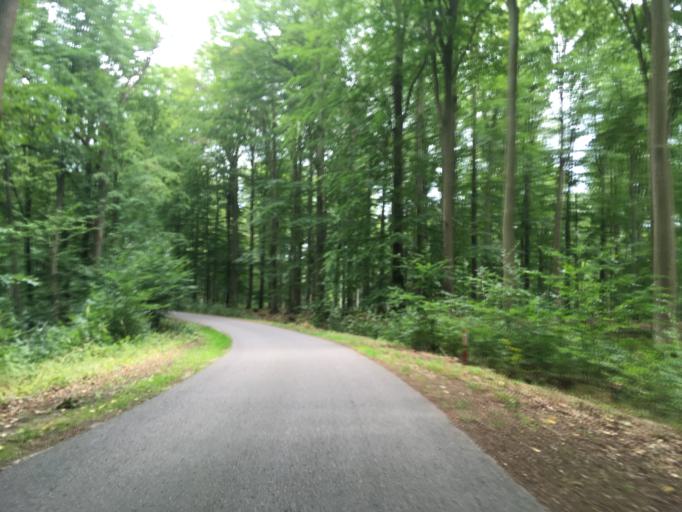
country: DE
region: Brandenburg
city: Althuttendorf
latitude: 53.0195
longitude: 13.7986
